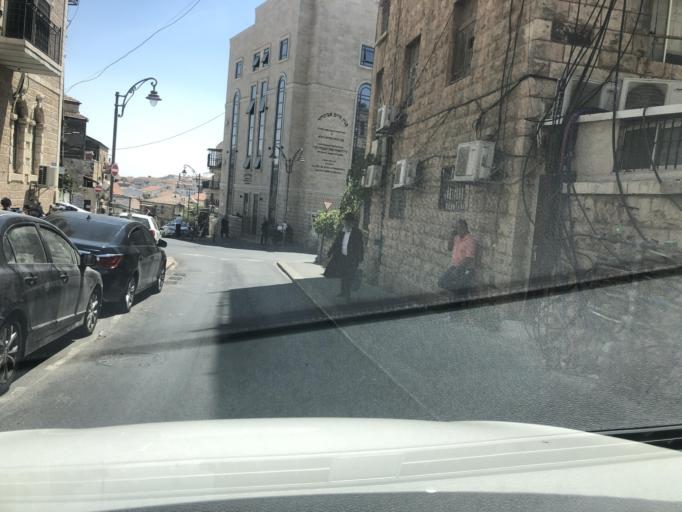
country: IL
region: Jerusalem
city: West Jerusalem
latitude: 31.7896
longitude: 35.2201
